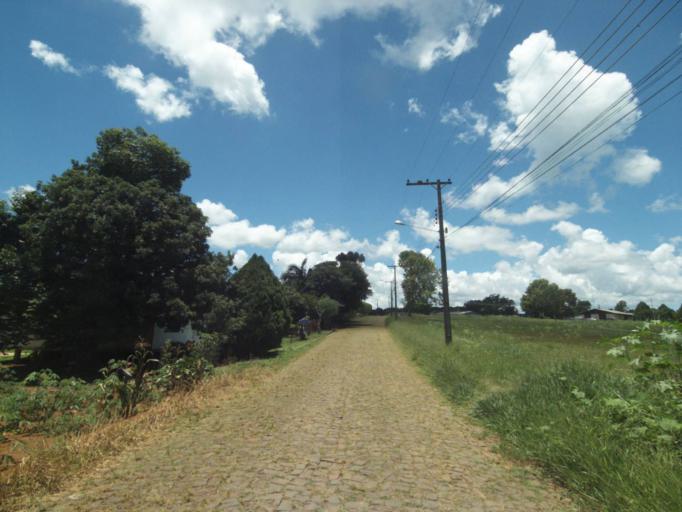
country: BR
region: Parana
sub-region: Pinhao
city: Pinhao
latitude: -25.7905
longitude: -52.0861
